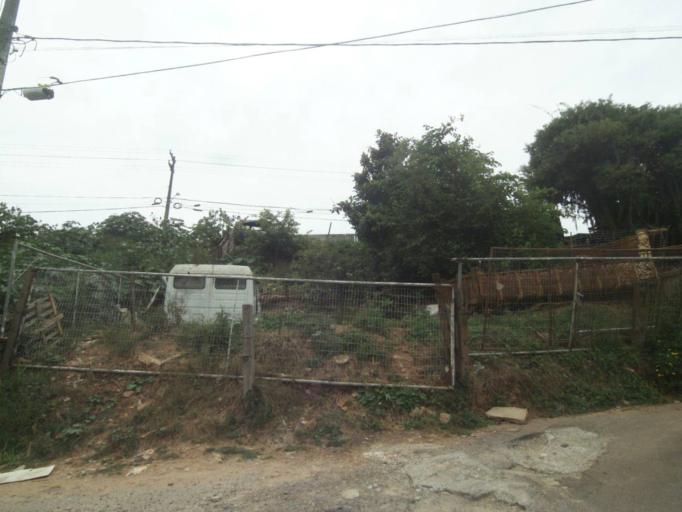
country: BR
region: Parana
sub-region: Curitiba
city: Curitiba
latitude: -25.5069
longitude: -49.3396
